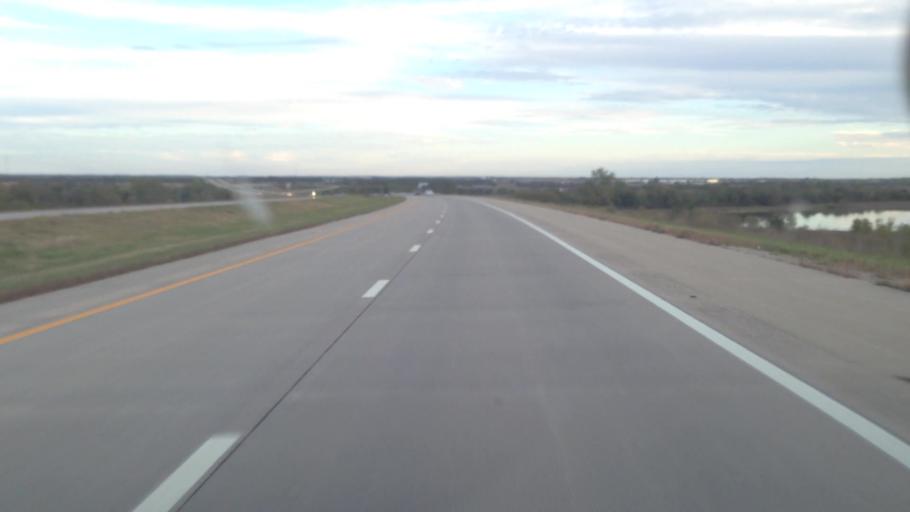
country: US
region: Kansas
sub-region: Franklin County
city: Ottawa
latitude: 38.6753
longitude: -95.2613
